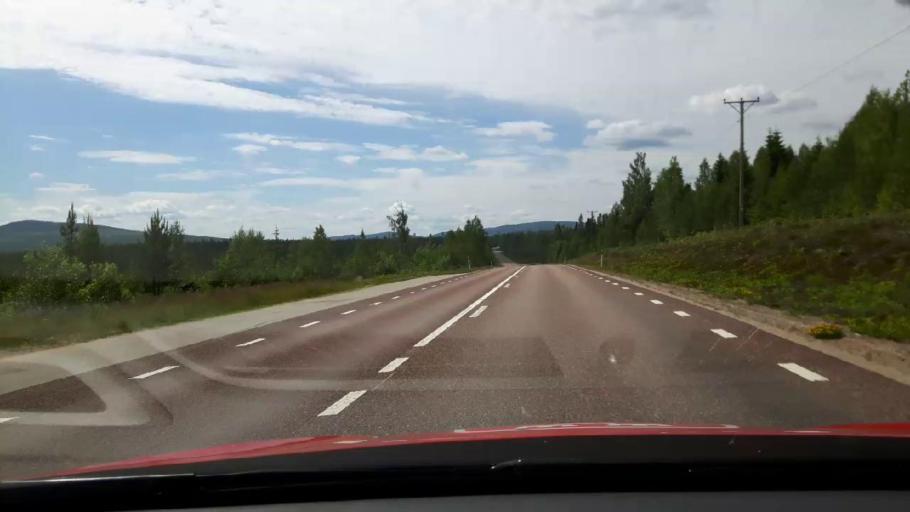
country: SE
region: Jaemtland
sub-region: Harjedalens Kommun
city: Sveg
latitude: 62.0615
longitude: 14.9144
